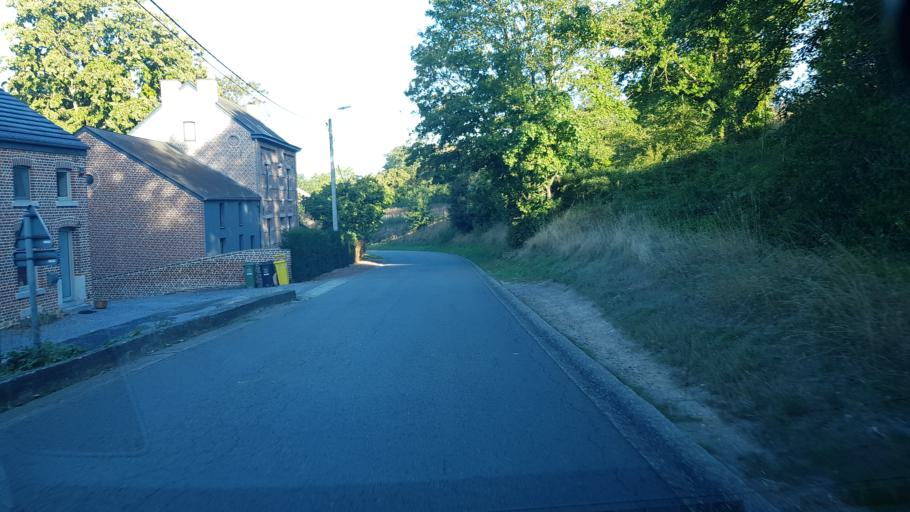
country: BE
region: Wallonia
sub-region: Province de Liege
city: Wanze
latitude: 50.5874
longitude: 5.1954
